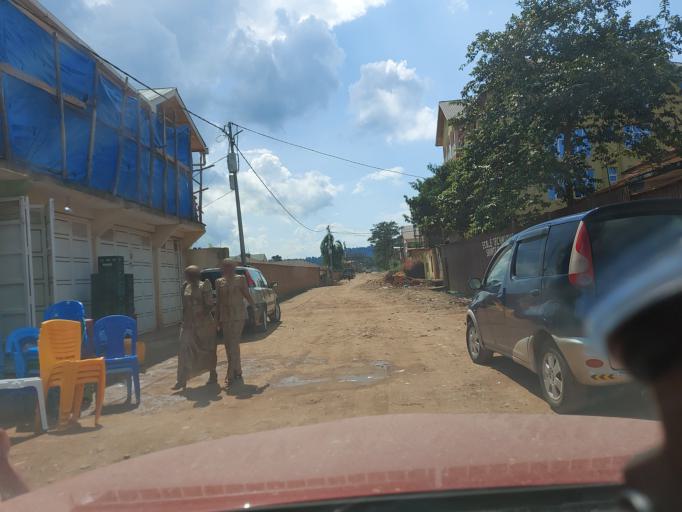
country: RW
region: Western Province
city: Cyangugu
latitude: -2.4996
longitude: 28.8827
